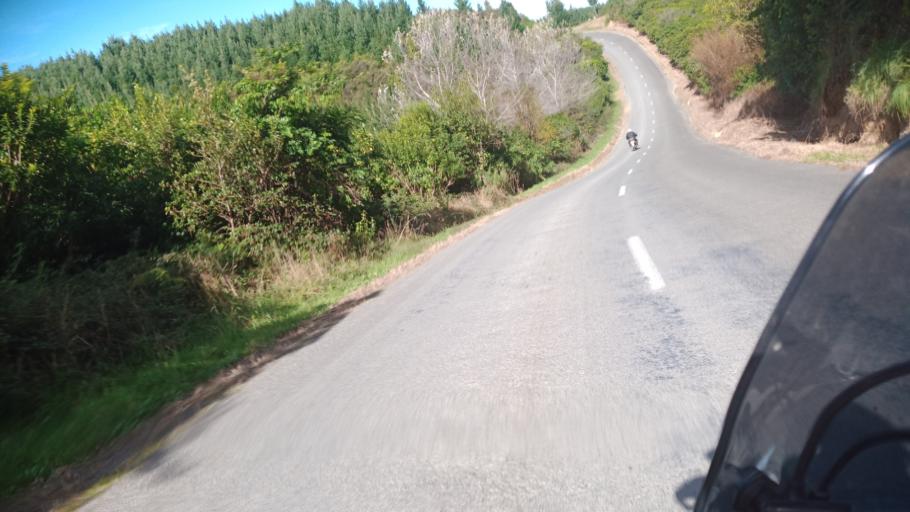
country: NZ
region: Hawke's Bay
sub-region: Wairoa District
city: Wairoa
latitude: -39.0070
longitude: 177.0966
